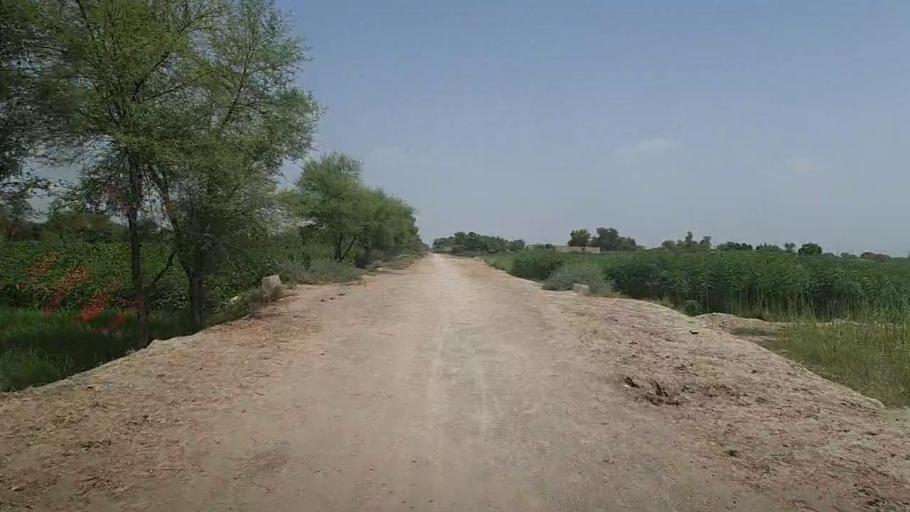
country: PK
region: Sindh
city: Pad Idan
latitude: 26.8444
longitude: 68.3200
